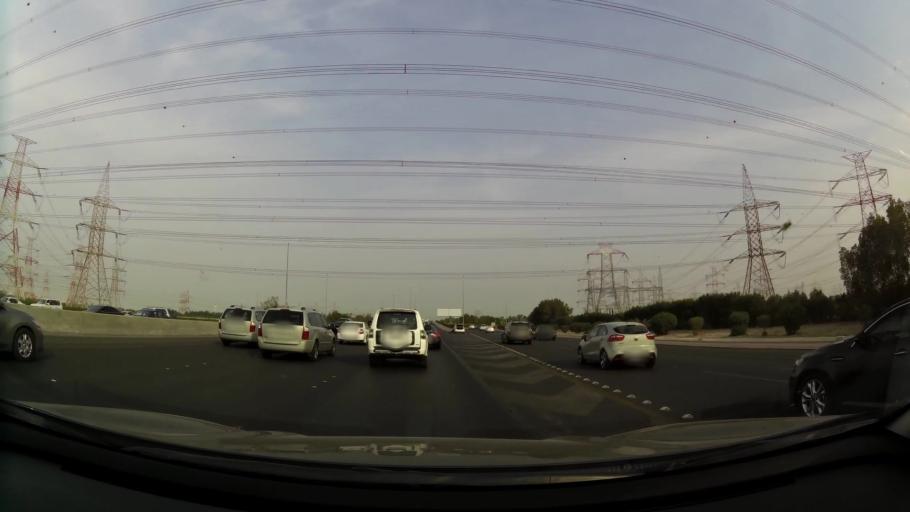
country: KW
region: Mubarak al Kabir
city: Sabah as Salim
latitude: 29.2647
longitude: 48.0353
